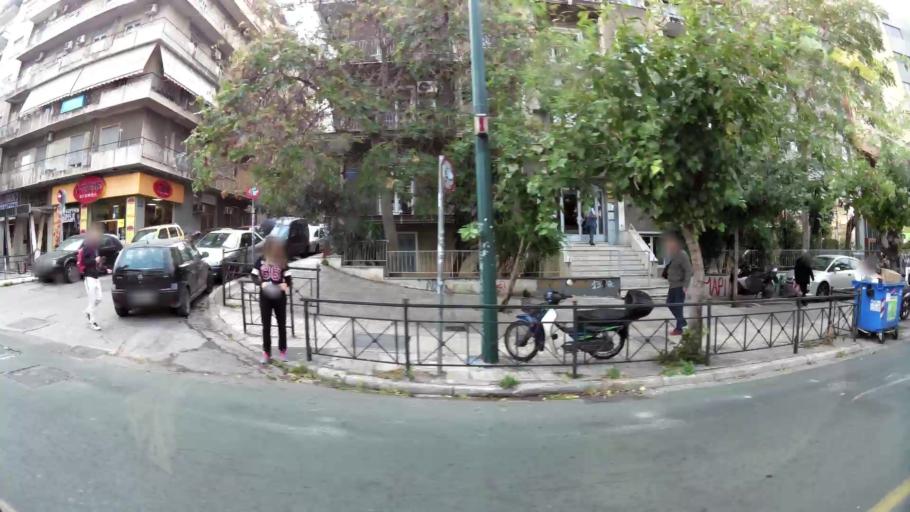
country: GR
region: Attica
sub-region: Nomarchia Athinas
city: Kipseli
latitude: 37.9885
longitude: 23.7505
